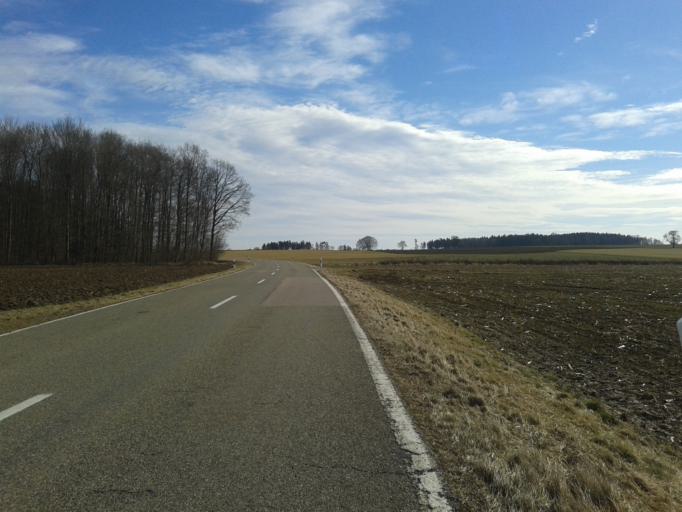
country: DE
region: Baden-Wuerttemberg
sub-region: Tuebingen Region
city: Altheim
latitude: 48.3006
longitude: 9.7680
